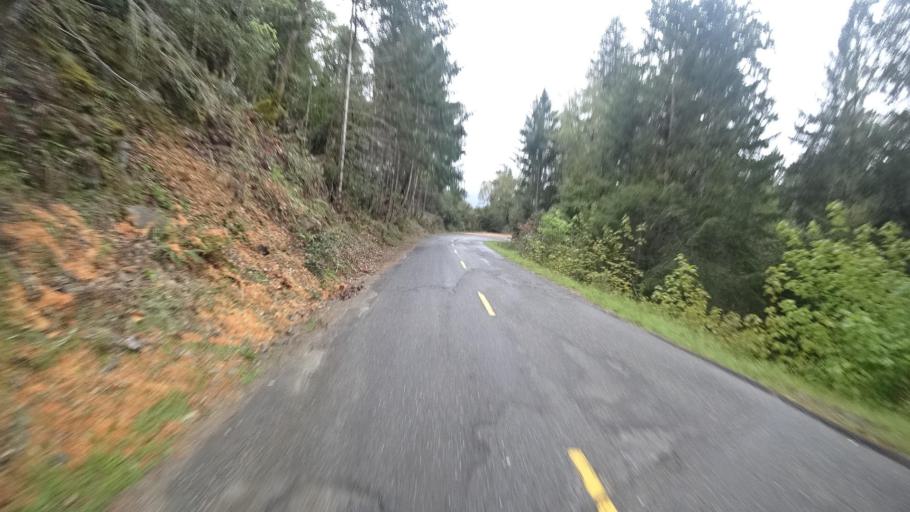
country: US
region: California
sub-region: Humboldt County
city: Redway
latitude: 40.2729
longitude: -123.7758
